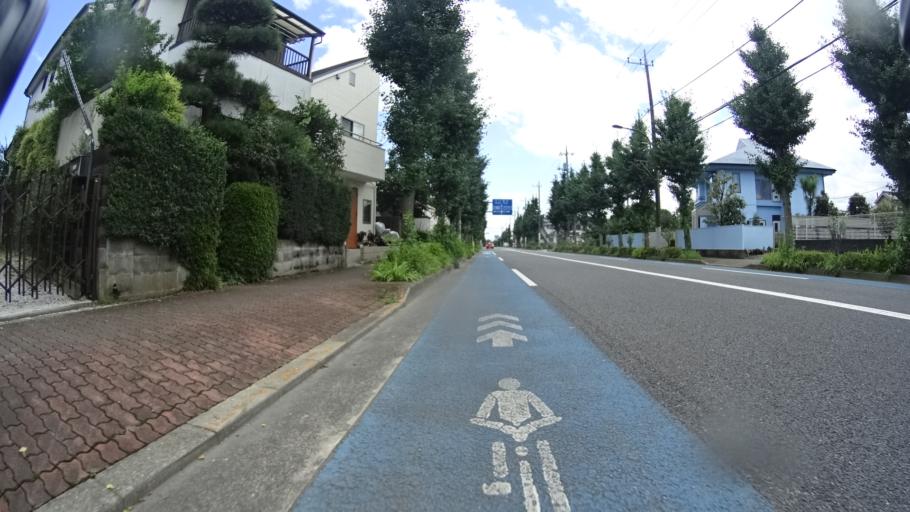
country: JP
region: Tokyo
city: Fussa
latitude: 35.7581
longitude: 139.3129
